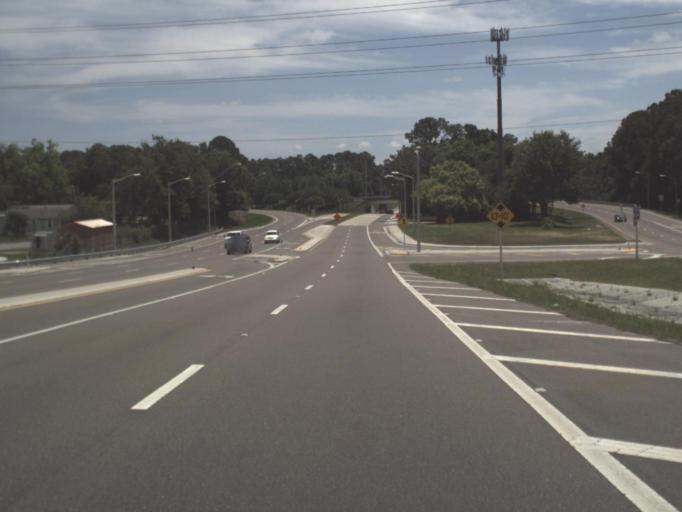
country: US
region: Florida
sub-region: Duval County
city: Jacksonville
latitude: 30.3597
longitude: -81.7132
